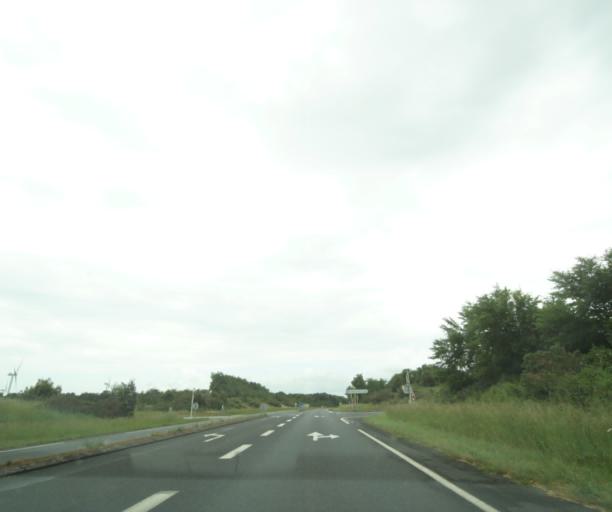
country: FR
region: Poitou-Charentes
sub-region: Departement des Deux-Sevres
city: Saint-Varent
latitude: 46.8584
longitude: -0.2089
